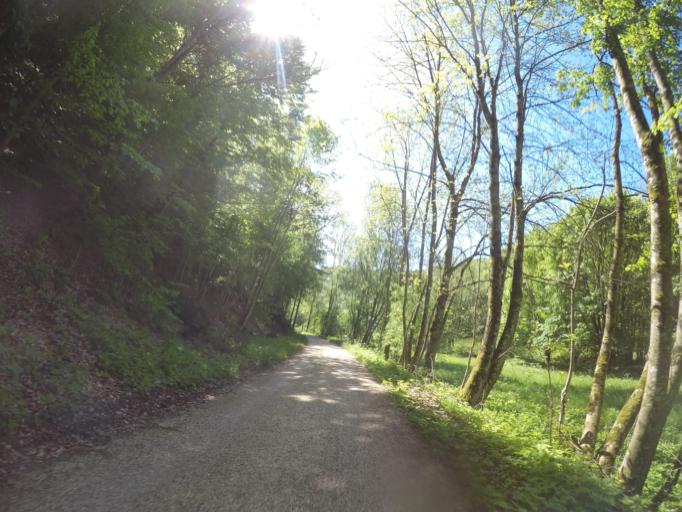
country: DE
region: Baden-Wuerttemberg
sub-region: Tuebingen Region
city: Blaubeuren
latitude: 48.3977
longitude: 9.7579
